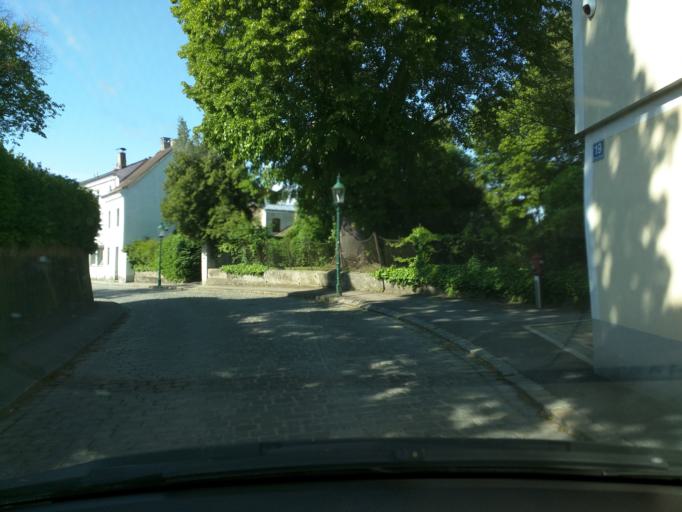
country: AT
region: Lower Austria
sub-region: Politischer Bezirk Melk
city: Ybbs an der Donau
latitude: 48.1757
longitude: 15.0868
